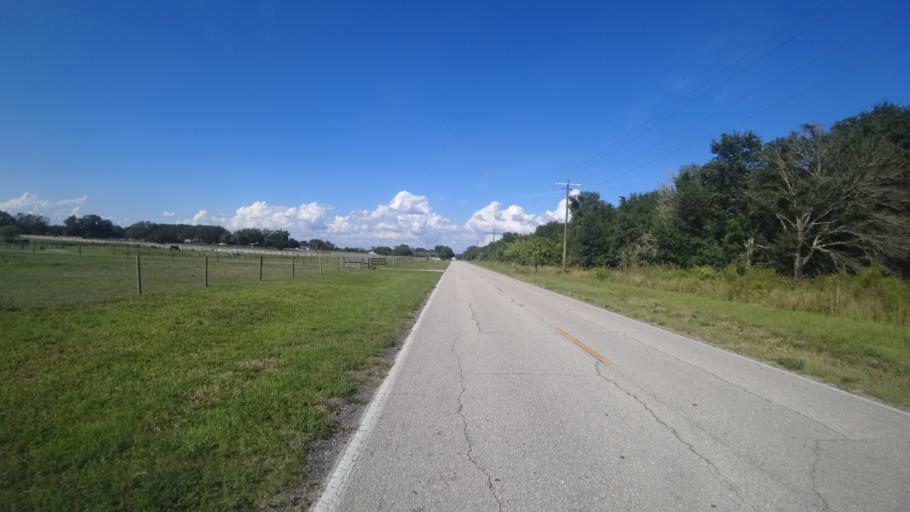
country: US
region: Florida
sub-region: Sarasota County
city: The Meadows
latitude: 27.4597
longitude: -82.2705
